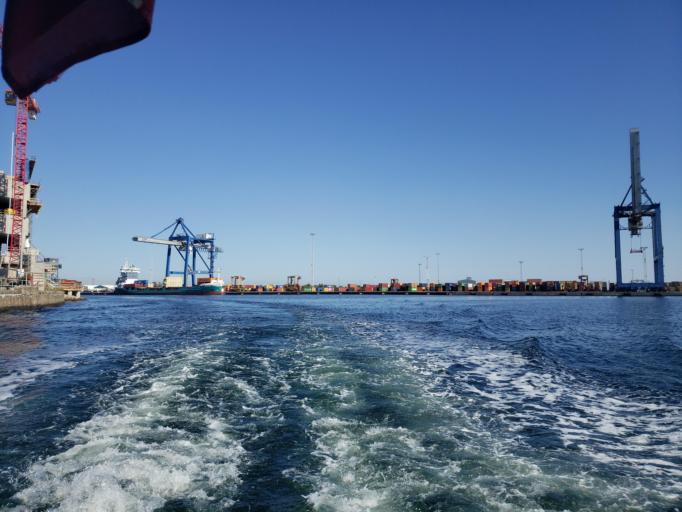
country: DK
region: Capital Region
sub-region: Kobenhavn
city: Christianshavn
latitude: 55.7076
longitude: 12.6060
